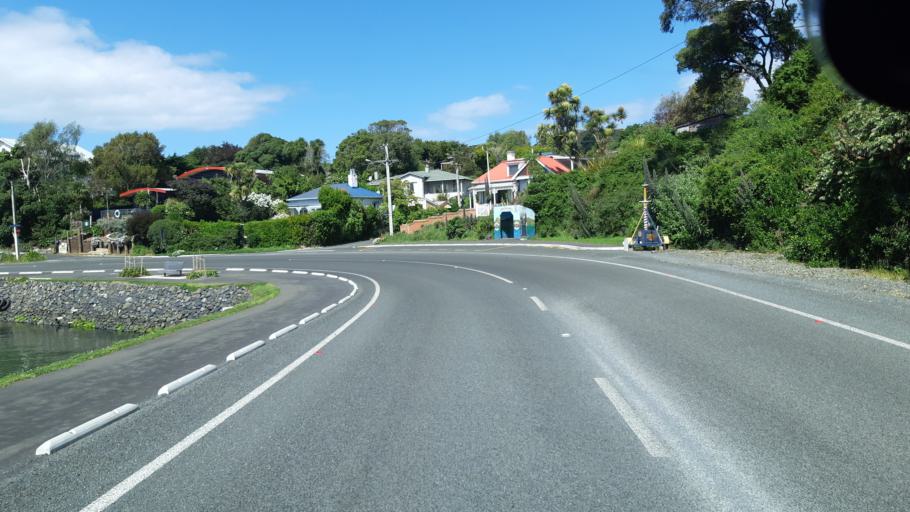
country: NZ
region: Otago
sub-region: Dunedin City
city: Portobello
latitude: -45.8381
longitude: 170.6438
